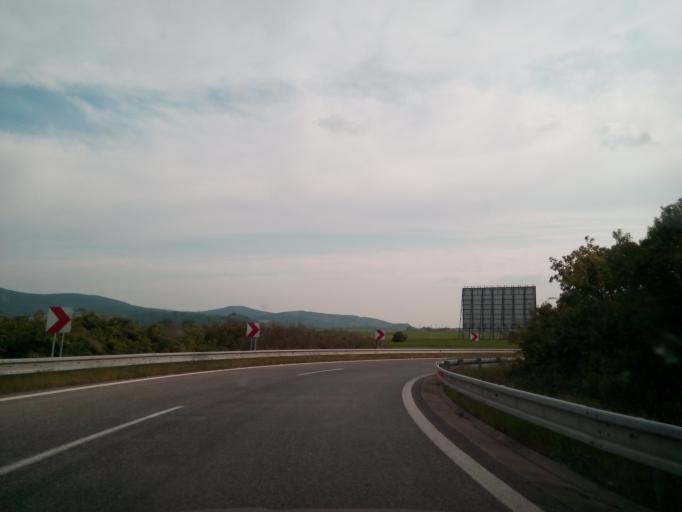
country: SK
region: Trenciansky
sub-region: Okres Trencin
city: Trencin
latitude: 48.8588
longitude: 17.9583
